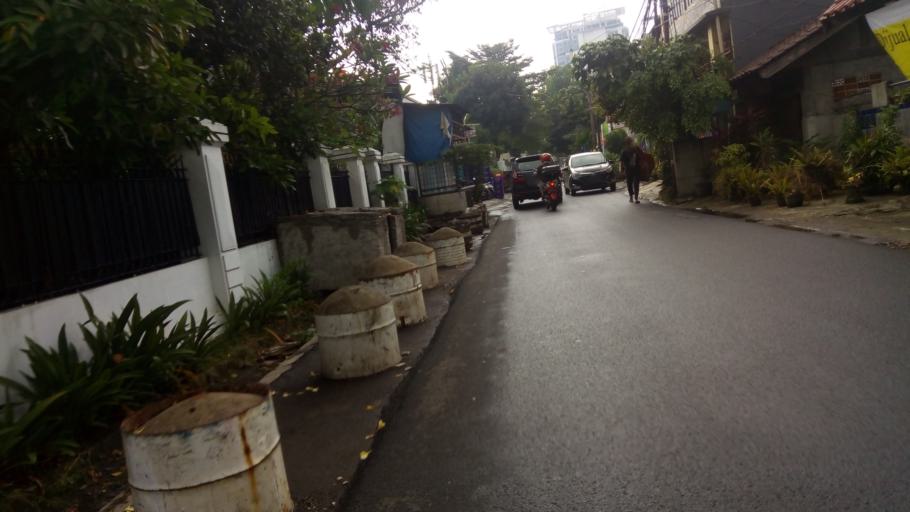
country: ID
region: Jakarta Raya
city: Jakarta
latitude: -6.2643
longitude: 106.8043
